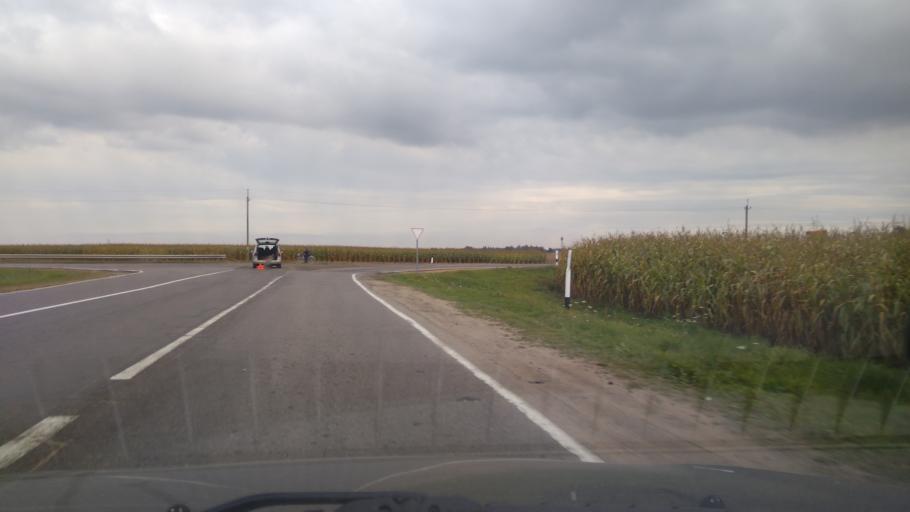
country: BY
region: Minsk
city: Dukora
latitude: 53.6554
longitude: 27.9436
